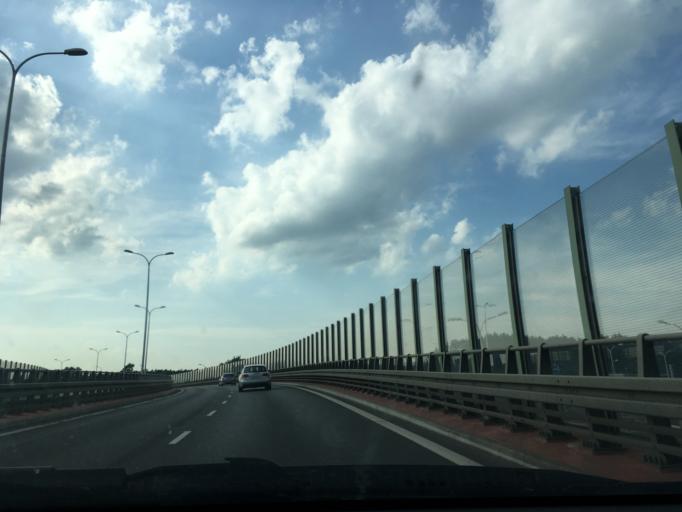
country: PL
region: Podlasie
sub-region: Bialystok
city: Bialystok
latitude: 53.1586
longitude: 23.1527
